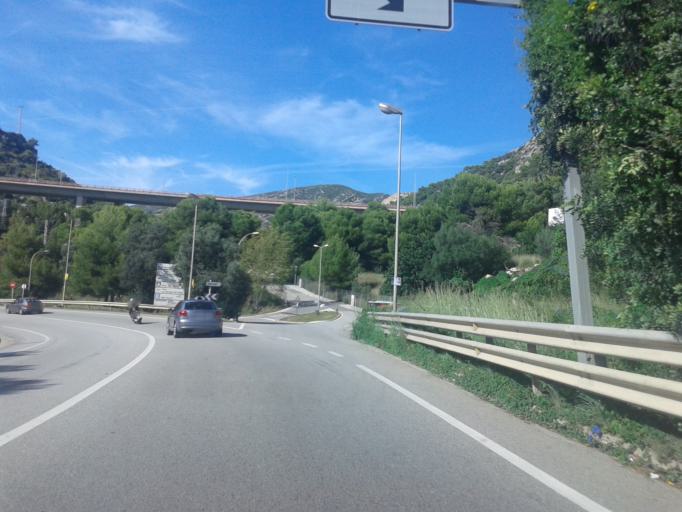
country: ES
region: Catalonia
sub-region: Provincia de Barcelona
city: Castelldefels
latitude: 41.2573
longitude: 1.9049
